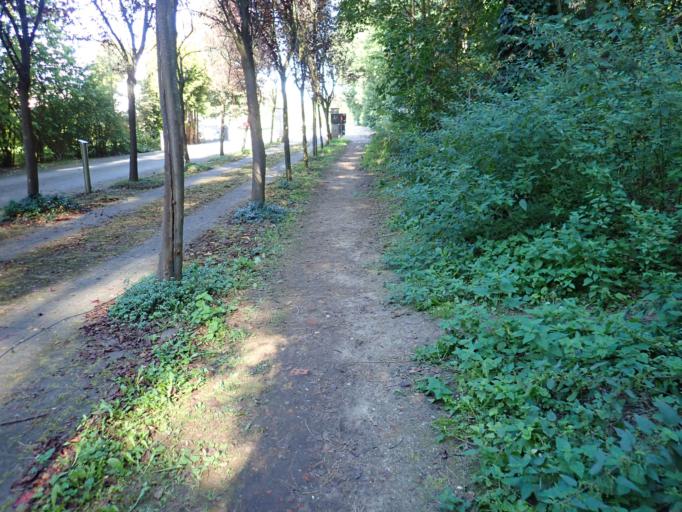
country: BE
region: Flanders
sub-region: Provincie Vlaams-Brabant
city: Oud-Heverlee
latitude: 50.8517
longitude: 4.6789
